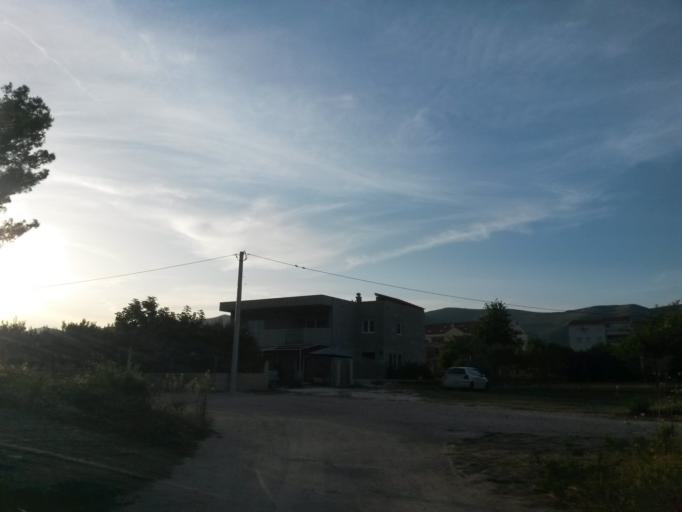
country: HR
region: Splitsko-Dalmatinska
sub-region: Grad Trogir
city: Trogir
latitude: 43.5435
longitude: 16.3214
